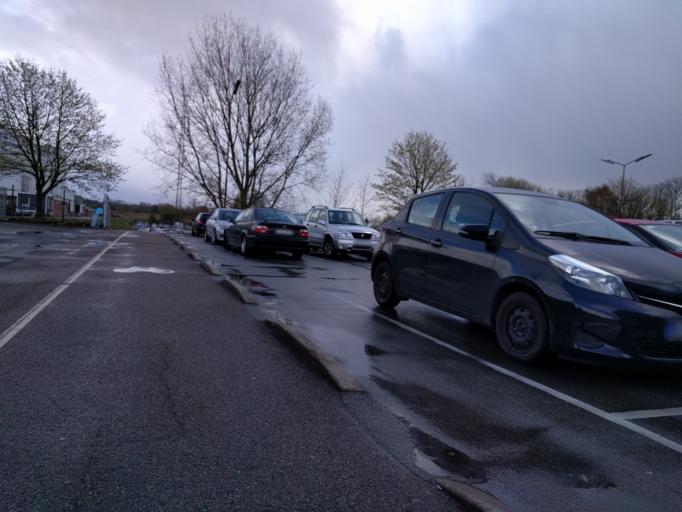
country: DK
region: South Denmark
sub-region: Kerteminde Kommune
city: Munkebo
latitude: 55.4670
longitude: 10.5403
